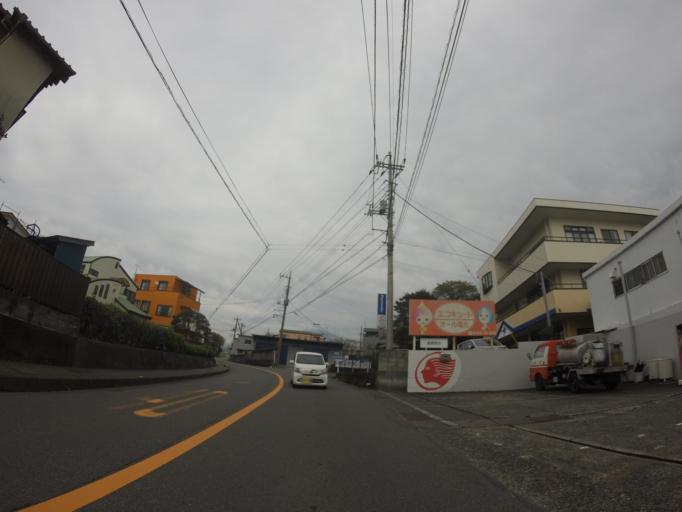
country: JP
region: Shizuoka
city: Fuji
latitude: 35.1826
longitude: 138.6640
